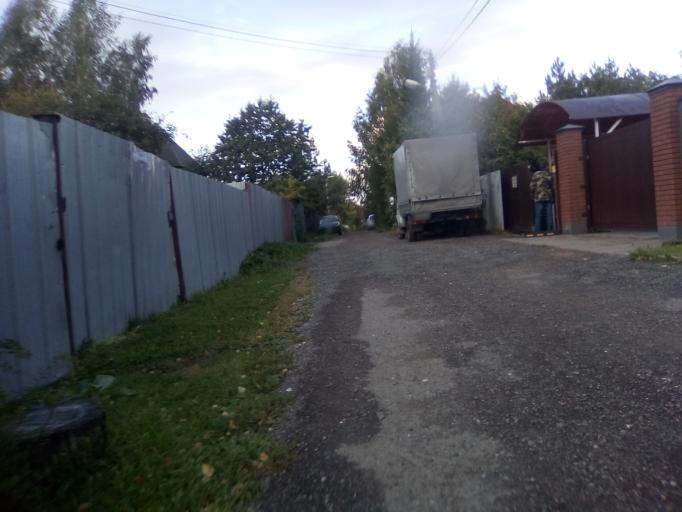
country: RU
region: Moskovskaya
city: Lesnoy Gorodok
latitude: 55.6301
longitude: 37.2199
